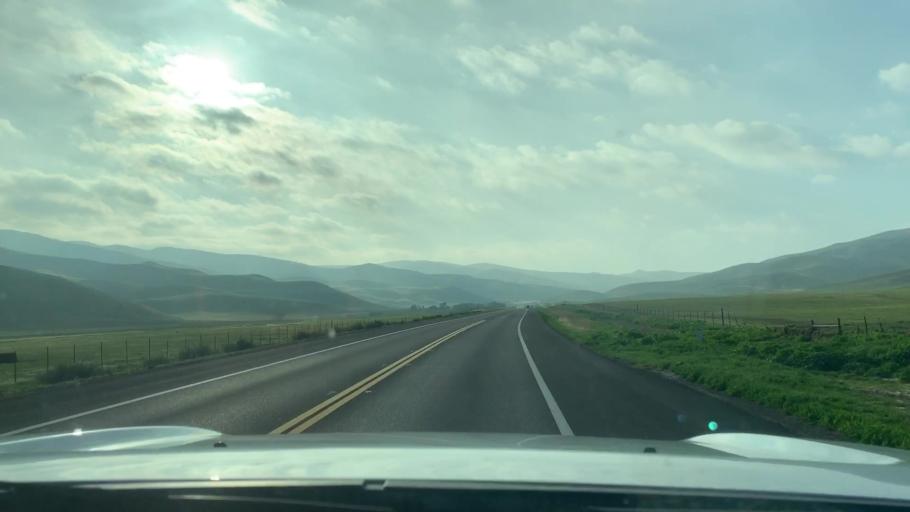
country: US
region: California
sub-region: Kings County
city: Avenal
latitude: 35.7841
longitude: -120.1196
